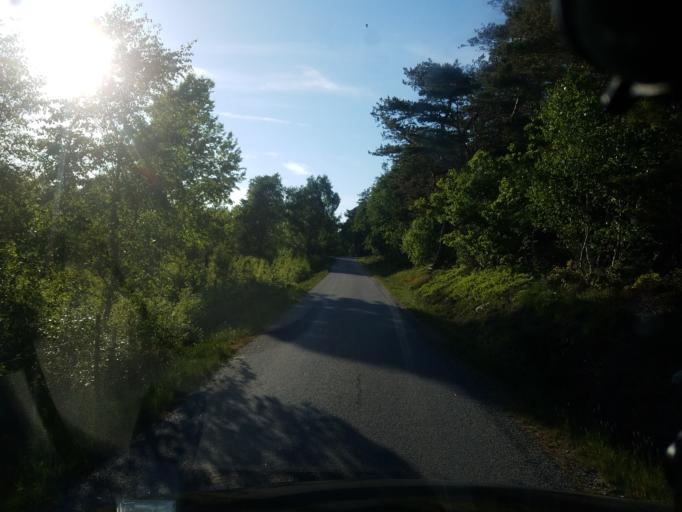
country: SE
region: Vaestra Goetaland
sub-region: Lysekils Kommun
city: Lysekil
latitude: 58.3015
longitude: 11.4666
